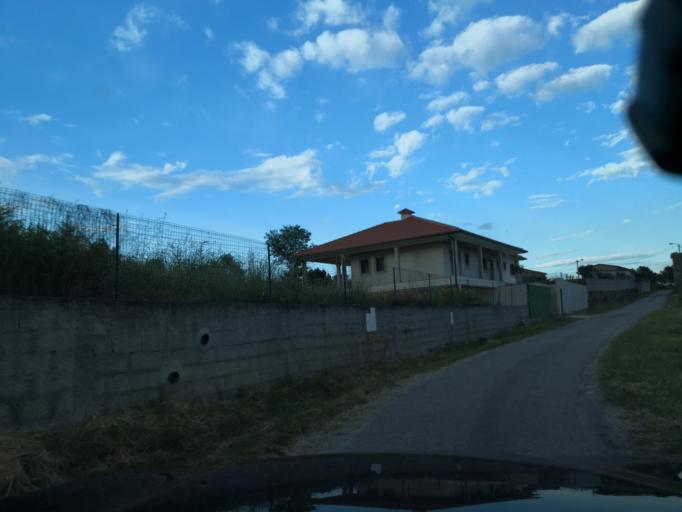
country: PT
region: Vila Real
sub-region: Vila Real
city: Vila Real
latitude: 41.2999
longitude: -7.7773
